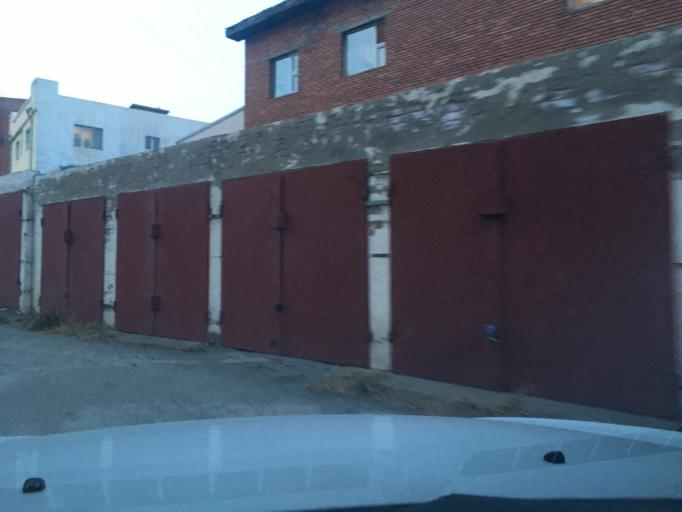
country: MN
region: Ulaanbaatar
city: Ulaanbaatar
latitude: 47.9158
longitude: 106.8569
